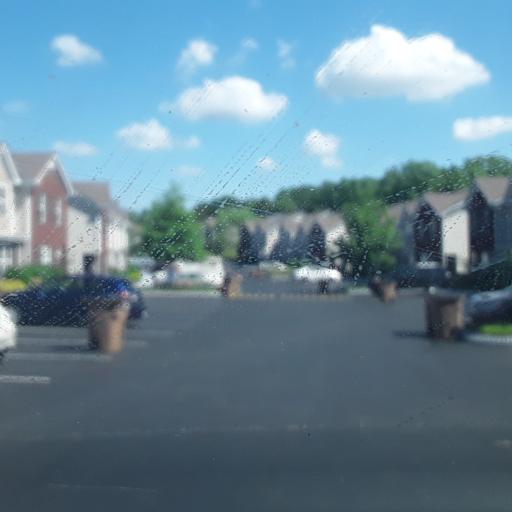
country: US
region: Tennessee
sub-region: Williamson County
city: Brentwood Estates
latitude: 36.0323
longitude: -86.7038
